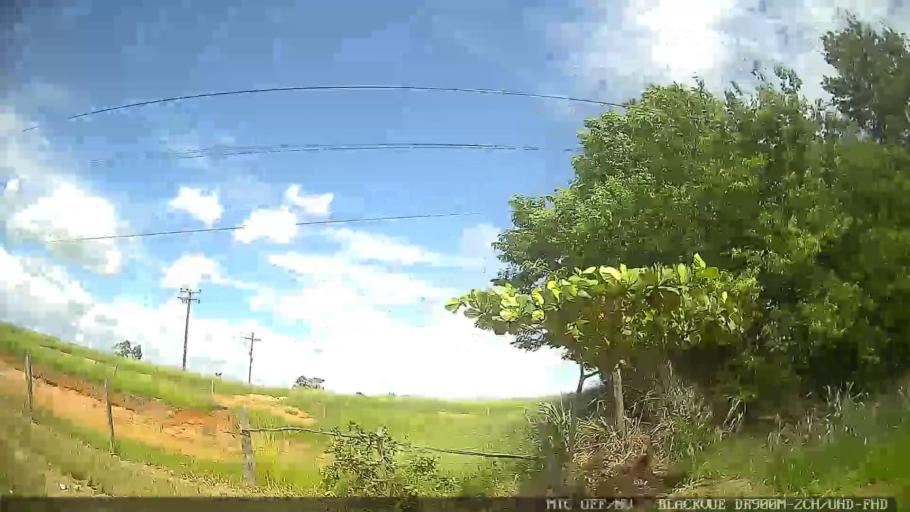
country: BR
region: Sao Paulo
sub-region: Conchas
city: Conchas
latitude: -23.0455
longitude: -48.0232
